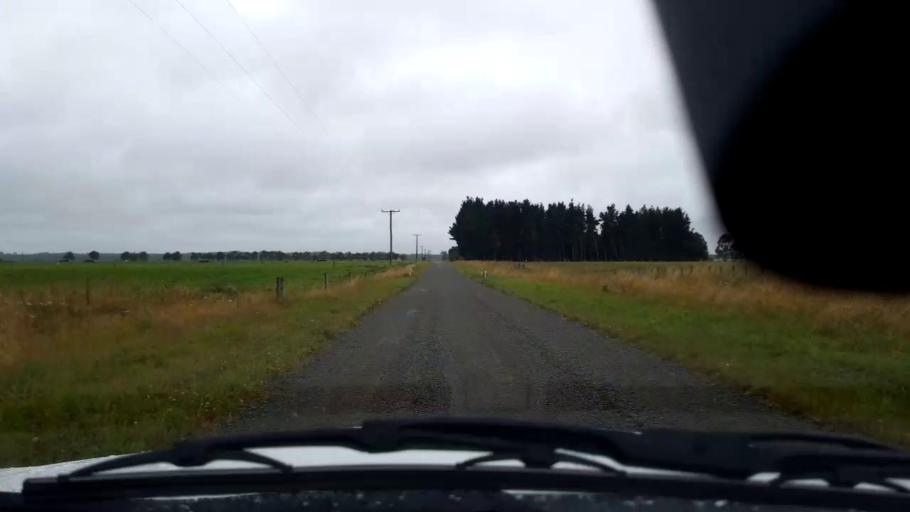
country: NZ
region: Canterbury
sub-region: Timaru District
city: Pleasant Point
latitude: -44.2394
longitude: 171.2018
